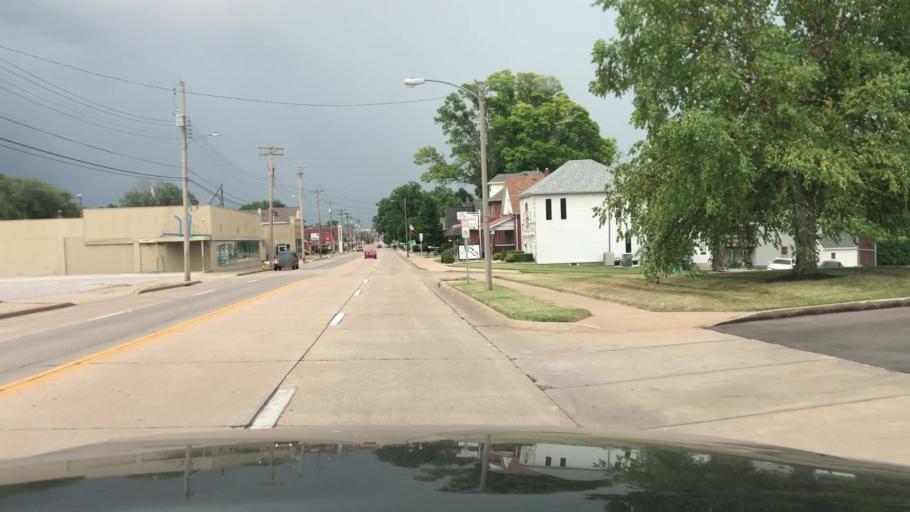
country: US
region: Missouri
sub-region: Saint Charles County
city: Saint Charles
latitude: 38.7841
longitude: -90.4964
